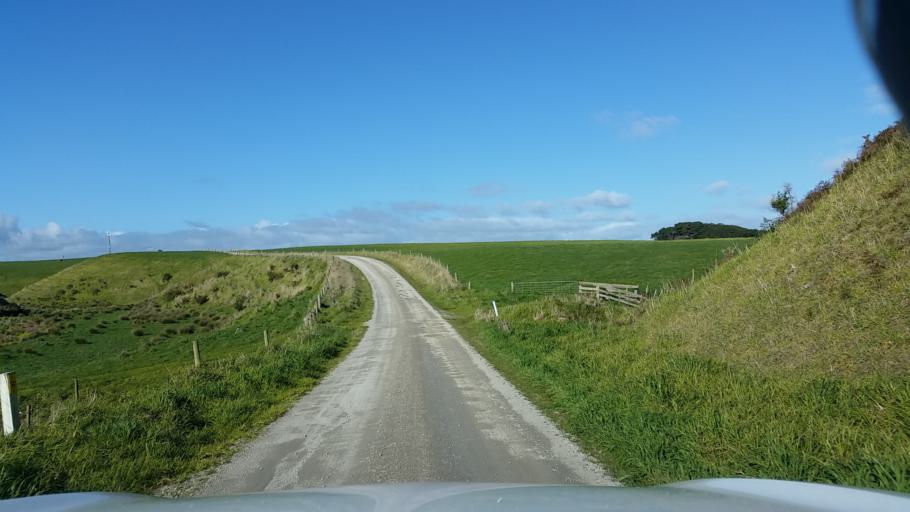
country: NZ
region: Taranaki
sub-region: South Taranaki District
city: Patea
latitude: -39.6838
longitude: 174.3915
